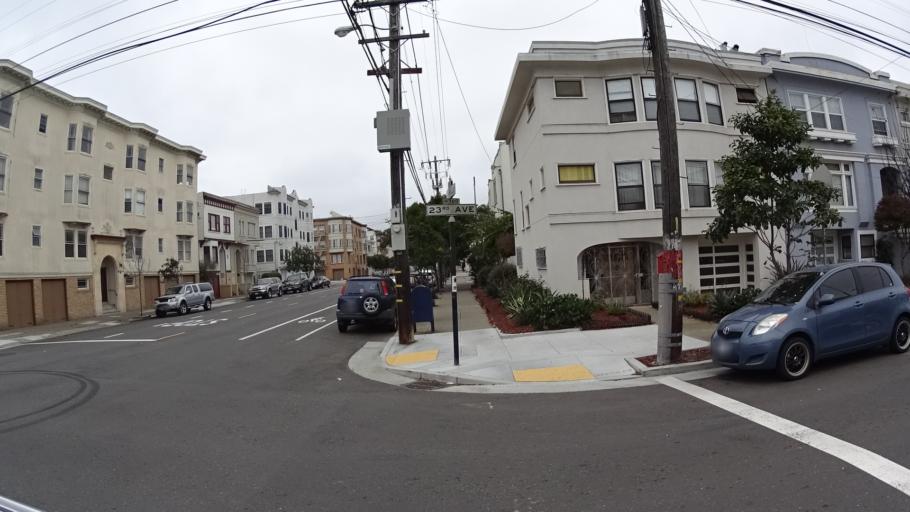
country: US
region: California
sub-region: San Francisco County
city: San Francisco
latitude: 37.7751
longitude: -122.4822
